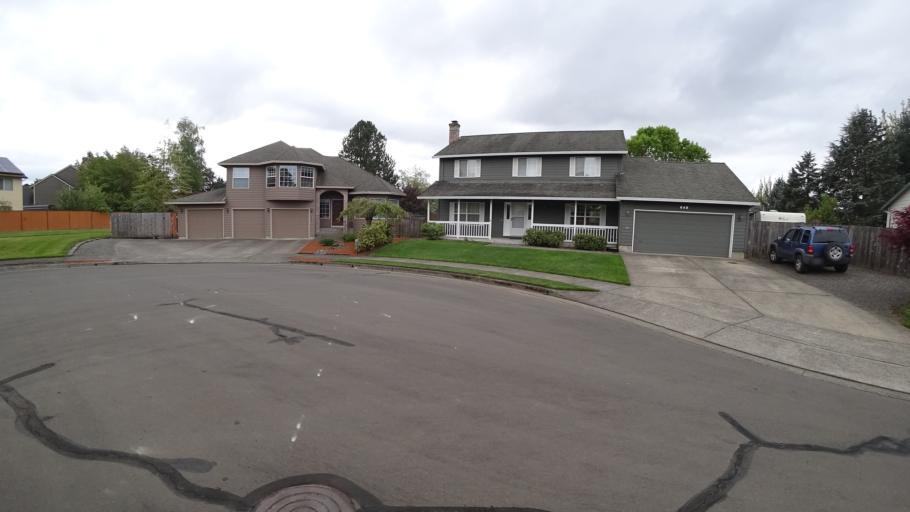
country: US
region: Oregon
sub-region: Washington County
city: Hillsboro
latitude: 45.5409
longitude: -122.9830
